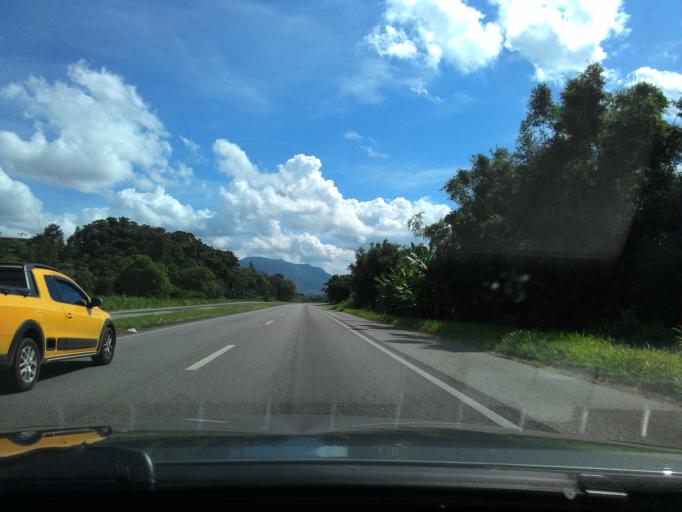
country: BR
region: Sao Paulo
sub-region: Jacupiranga
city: Jacupiranga
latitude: -24.7202
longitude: -48.0411
